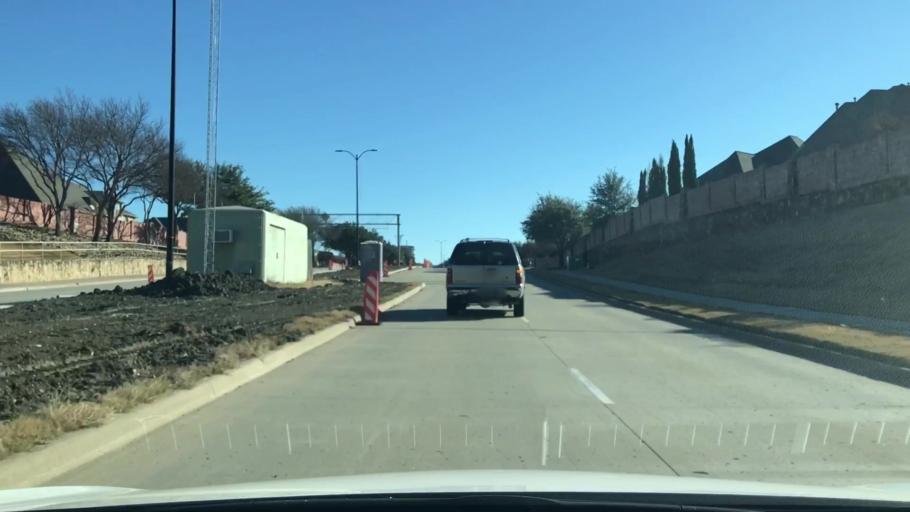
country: US
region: Texas
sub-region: Collin County
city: Frisco
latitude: 33.1149
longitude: -96.8480
